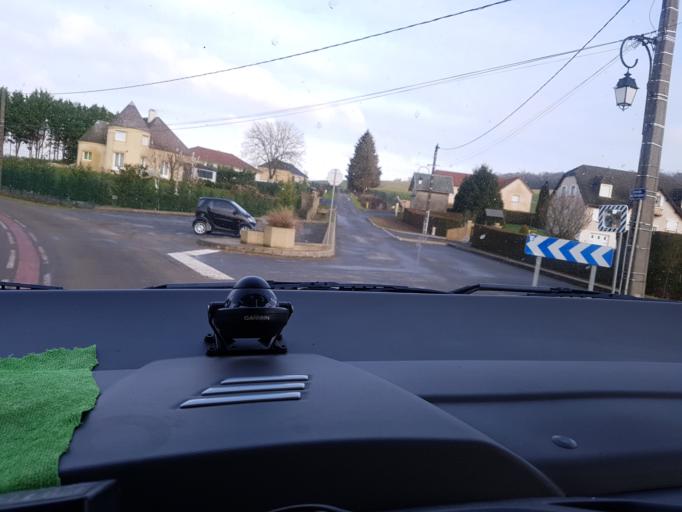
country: FR
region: Champagne-Ardenne
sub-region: Departement des Ardennes
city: Tournes
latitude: 49.7493
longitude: 4.6124
